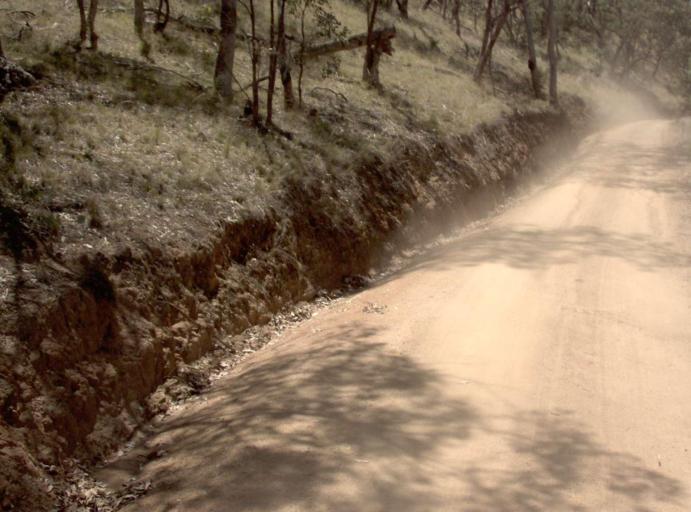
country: AU
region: New South Wales
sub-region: Snowy River
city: Jindabyne
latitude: -37.0967
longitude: 148.3711
